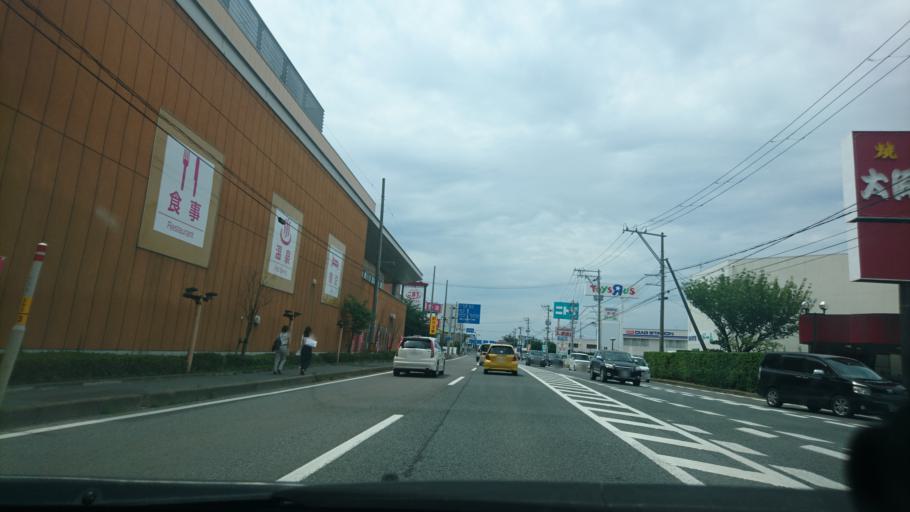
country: JP
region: Akita
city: Akita
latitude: 39.7016
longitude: 140.1089
